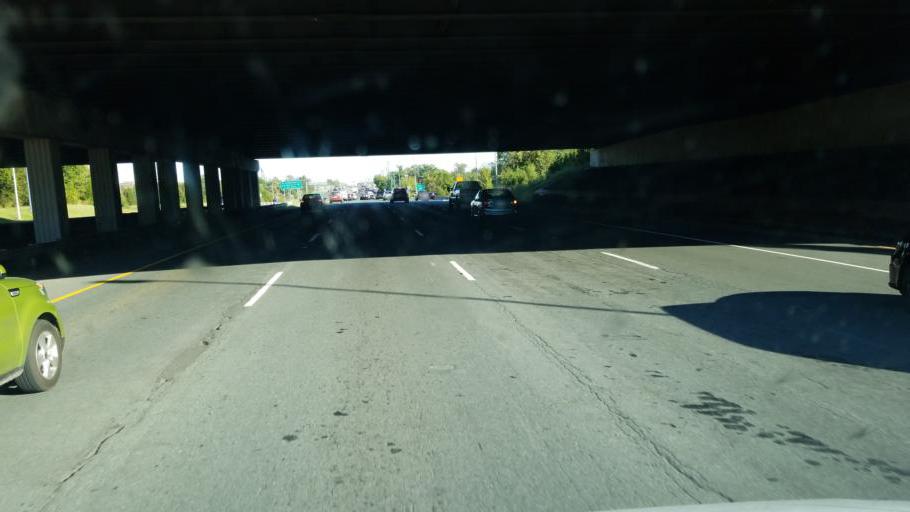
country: US
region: Virginia
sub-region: Fairfax County
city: Chantilly
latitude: 38.8976
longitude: -77.4398
